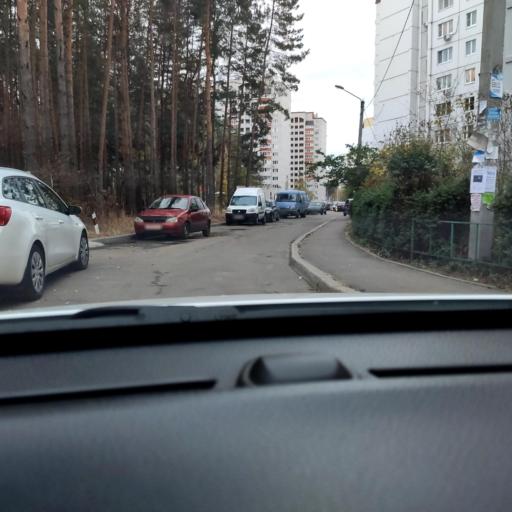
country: RU
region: Voronezj
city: Somovo
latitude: 51.6922
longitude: 39.2818
